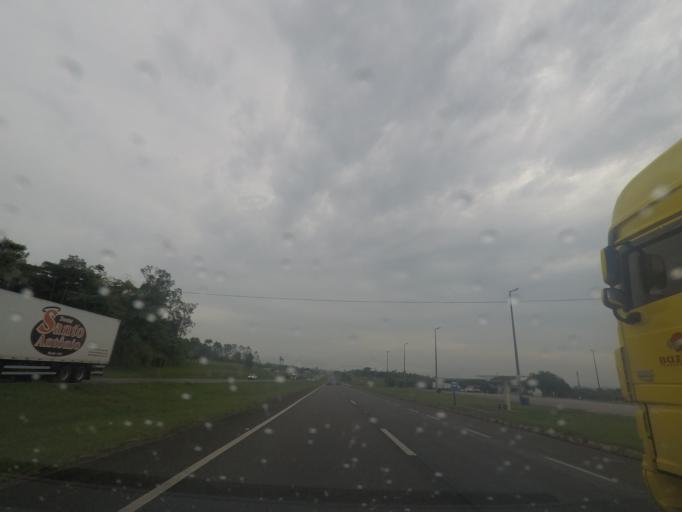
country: BR
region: Sao Paulo
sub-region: Pariquera-Acu
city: Pariquera Acu
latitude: -24.6266
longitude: -47.8999
